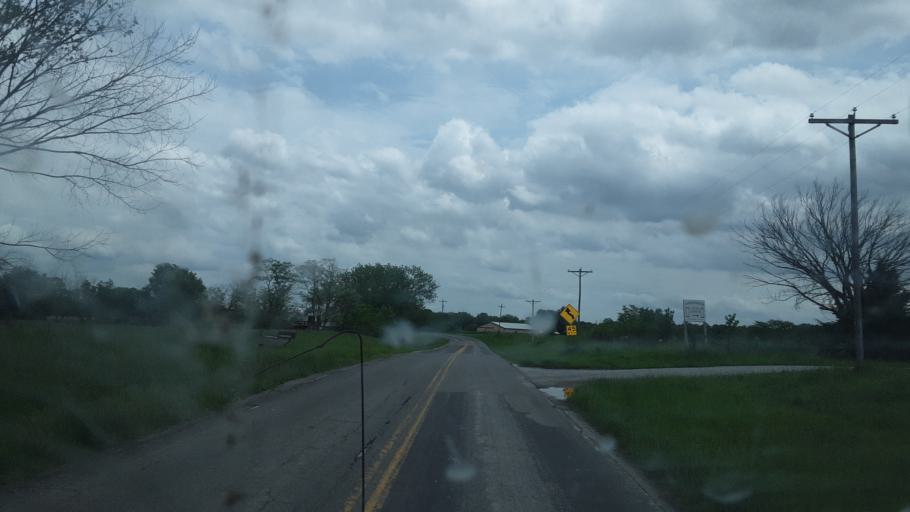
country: US
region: Missouri
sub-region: Clark County
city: Kahoka
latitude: 40.4412
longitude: -91.6059
